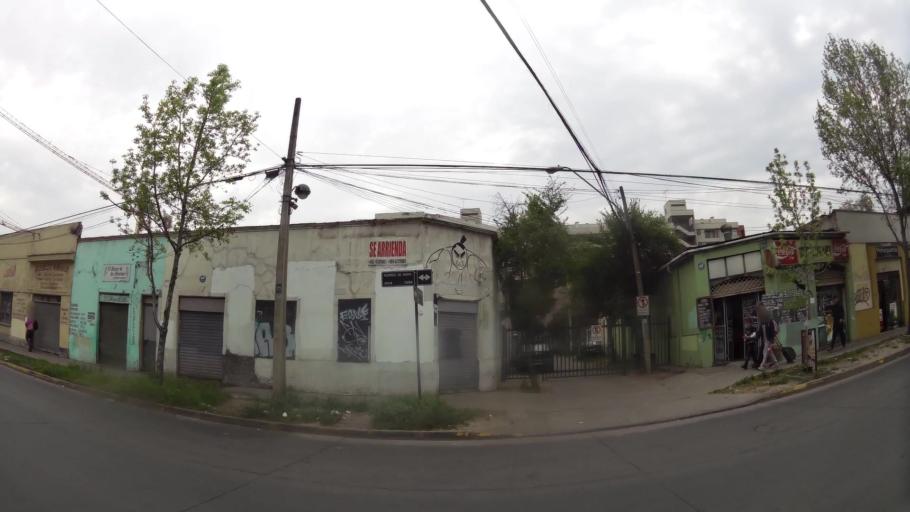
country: CL
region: Santiago Metropolitan
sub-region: Provincia de Santiago
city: Villa Presidente Frei, Nunoa, Santiago, Chile
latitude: -33.4738
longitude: -70.5995
